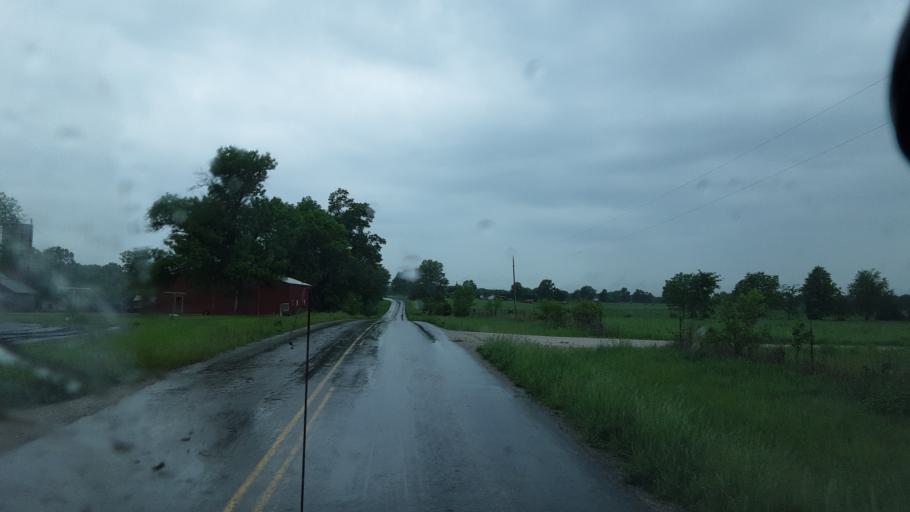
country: US
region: Missouri
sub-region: Randolph County
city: Moberly
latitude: 39.3683
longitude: -92.2618
